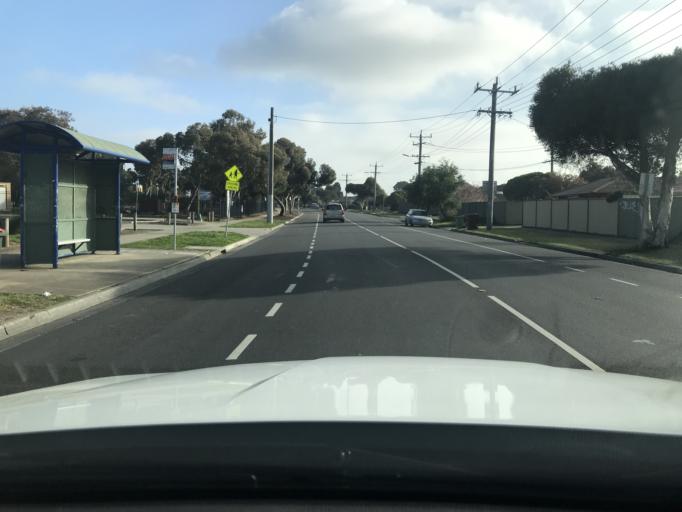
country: AU
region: Victoria
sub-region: Hume
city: Craigieburn
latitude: -37.6100
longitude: 144.9362
